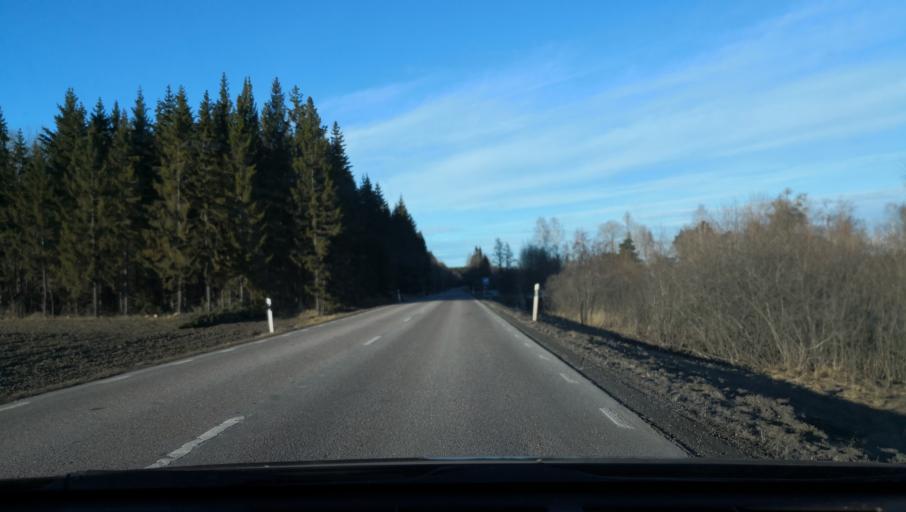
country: SE
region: Uppsala
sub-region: Osthammars Kommun
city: Gimo
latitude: 60.1853
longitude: 18.1902
